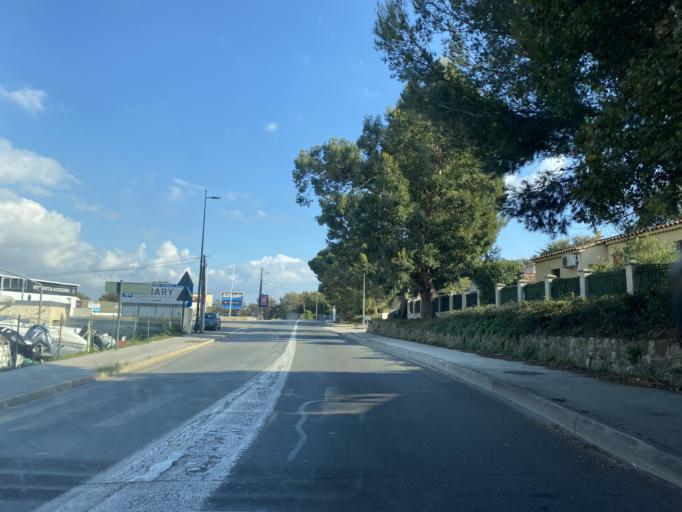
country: FR
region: Provence-Alpes-Cote d'Azur
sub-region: Departement du Var
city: Six-Fours-les-Plages
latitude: 43.1083
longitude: 5.8371
